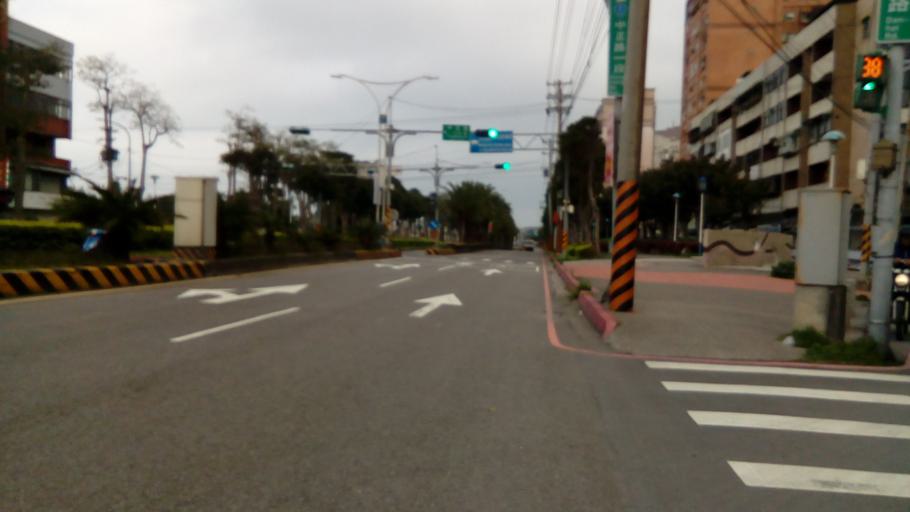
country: TW
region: Taipei
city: Taipei
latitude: 25.1776
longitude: 121.4247
